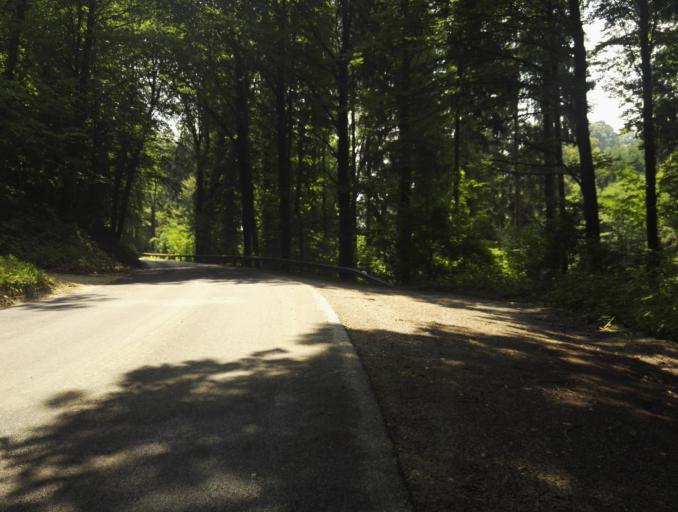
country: AT
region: Styria
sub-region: Politischer Bezirk Graz-Umgebung
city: Gratwein
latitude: 47.0898
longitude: 15.3151
